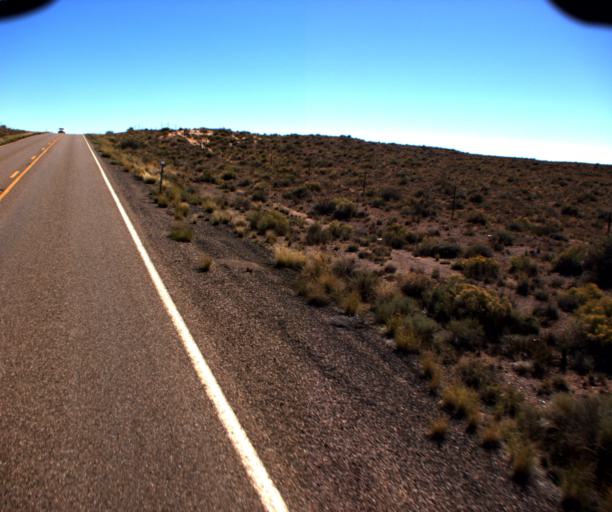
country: US
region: Arizona
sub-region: Navajo County
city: Holbrook
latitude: 35.0482
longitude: -110.0944
